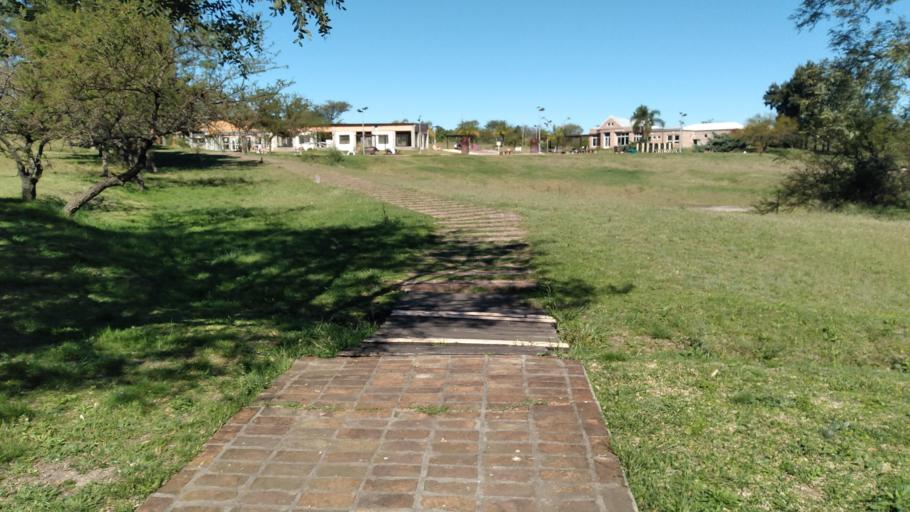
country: AR
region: Entre Rios
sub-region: Departamento de La Paz
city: La Paz
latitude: -30.7571
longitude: -59.6573
